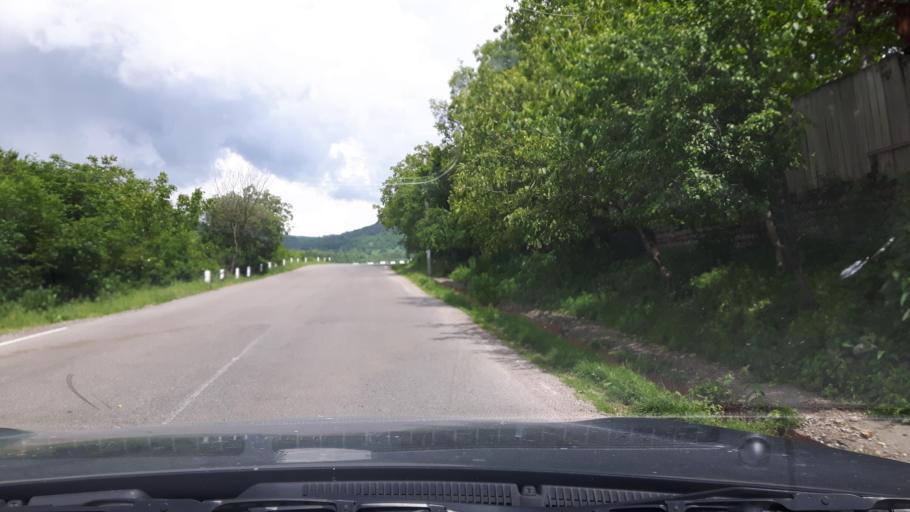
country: GE
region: Kakheti
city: Sagarejo
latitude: 41.8581
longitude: 45.2111
